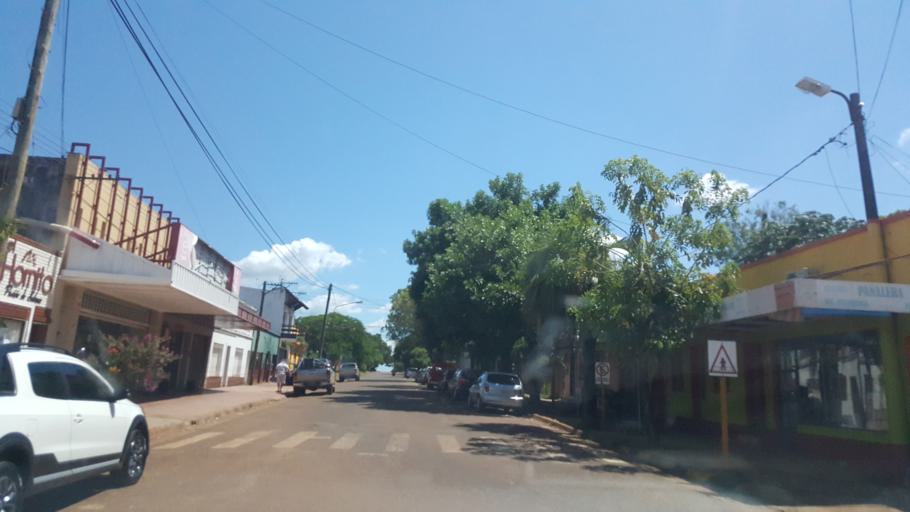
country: AR
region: Corrientes
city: Santo Tome
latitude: -28.5466
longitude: -56.0440
